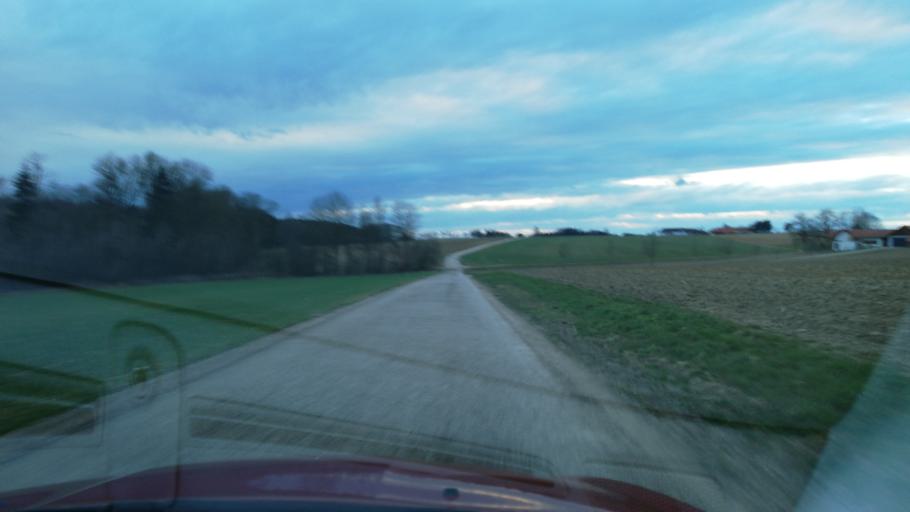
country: AT
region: Upper Austria
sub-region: Wels-Land
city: Buchkirchen
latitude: 48.2076
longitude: 14.0323
